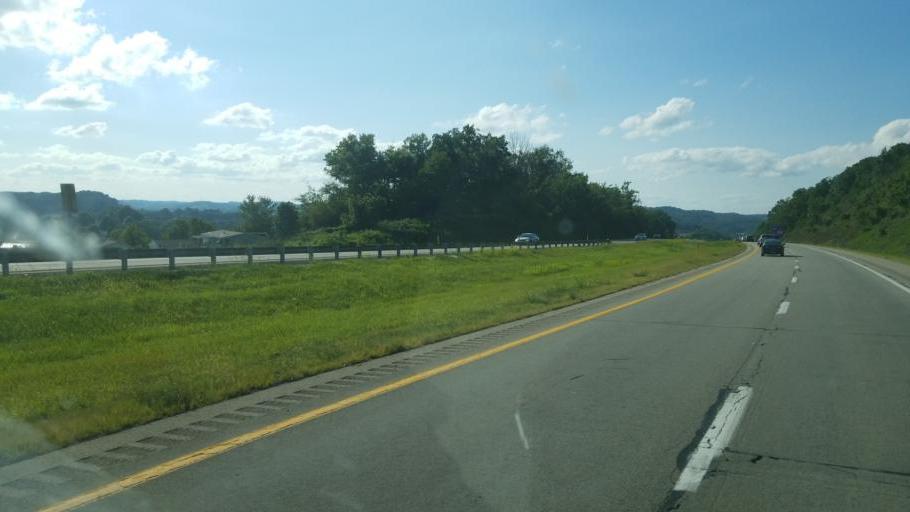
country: US
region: Pennsylvania
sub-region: Greene County
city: Morrisville
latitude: 39.8907
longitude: -80.1351
